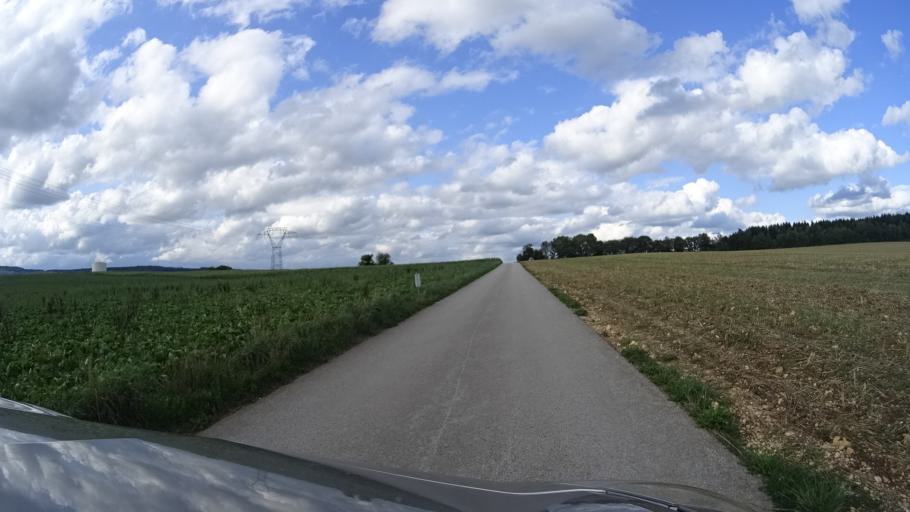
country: FR
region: Franche-Comte
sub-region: Departement du Doubs
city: Saone
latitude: 47.2182
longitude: 6.1309
